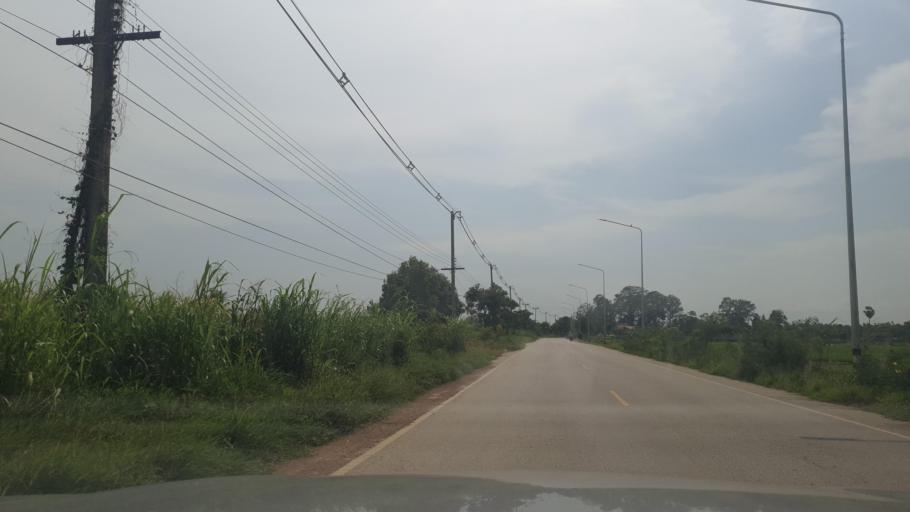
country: TH
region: Sukhothai
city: Si Samrong
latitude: 17.1404
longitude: 99.8371
